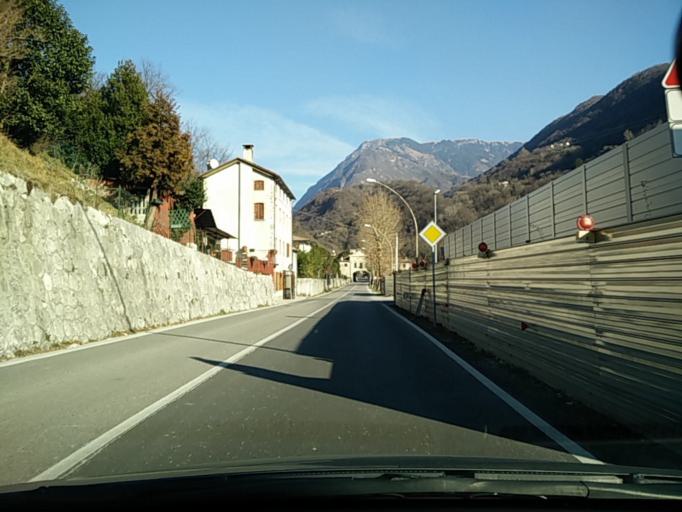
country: IT
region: Veneto
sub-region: Provincia di Treviso
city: Revine
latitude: 46.0092
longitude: 12.2864
